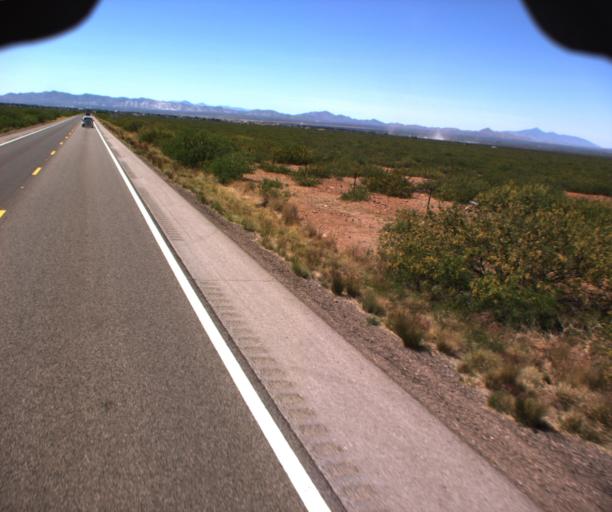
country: US
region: Arizona
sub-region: Cochise County
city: Douglas
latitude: 31.3982
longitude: -109.5063
